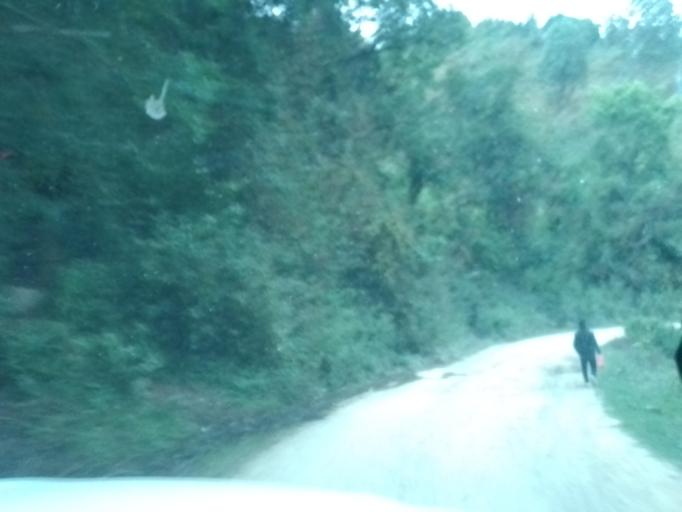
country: MX
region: Chiapas
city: Motozintla de Mendoza
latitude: 15.2175
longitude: -92.2398
